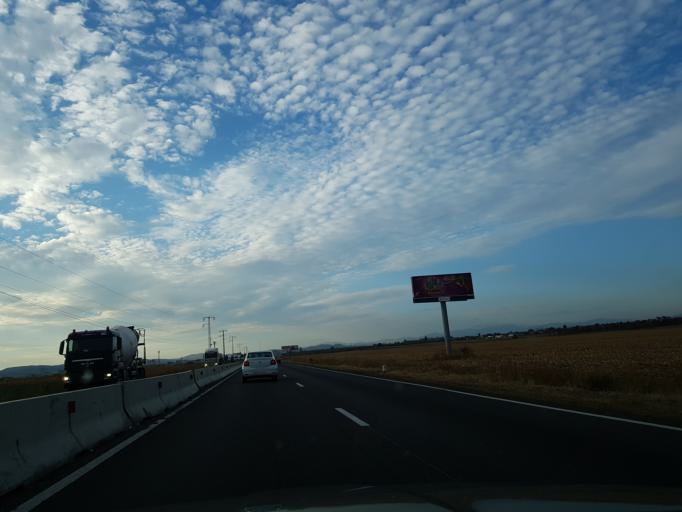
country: RO
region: Prahova
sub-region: Oras Baicoi
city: Baicoi
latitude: 45.0162
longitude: 25.8534
